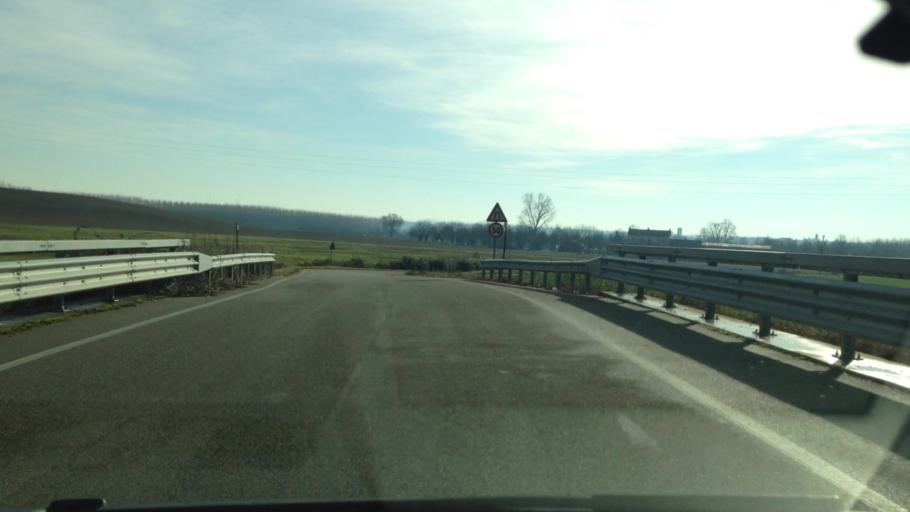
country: IT
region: Piedmont
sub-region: Provincia di Alessandria
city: Quattordio
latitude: 44.8907
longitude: 8.4048
